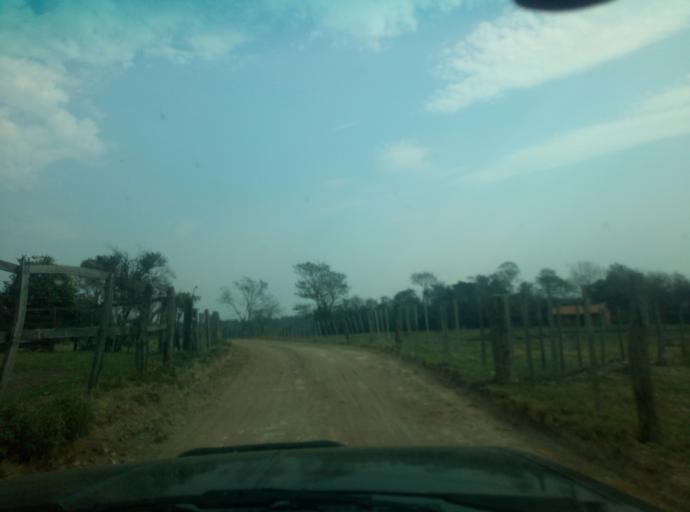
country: PY
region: Caaguazu
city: San Joaquin
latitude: -25.0908
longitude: -56.1409
